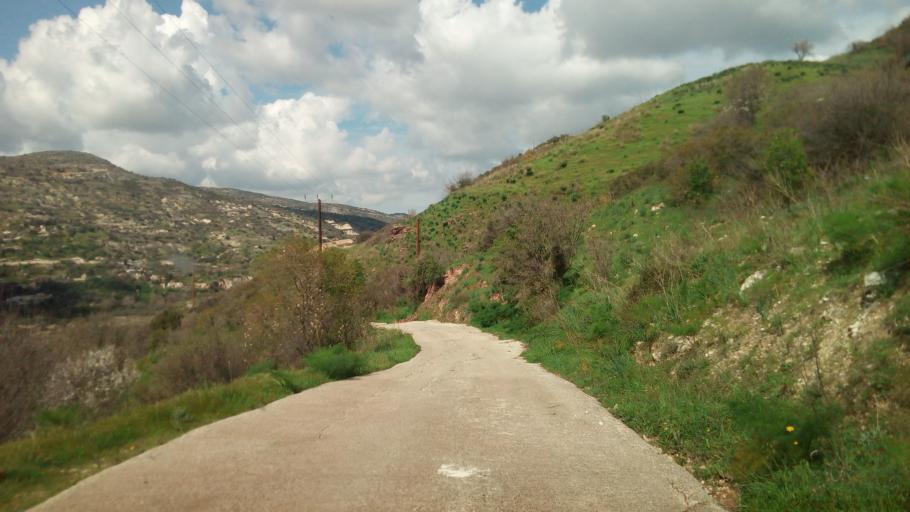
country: CY
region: Pafos
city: Mesogi
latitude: 34.7920
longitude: 32.5353
